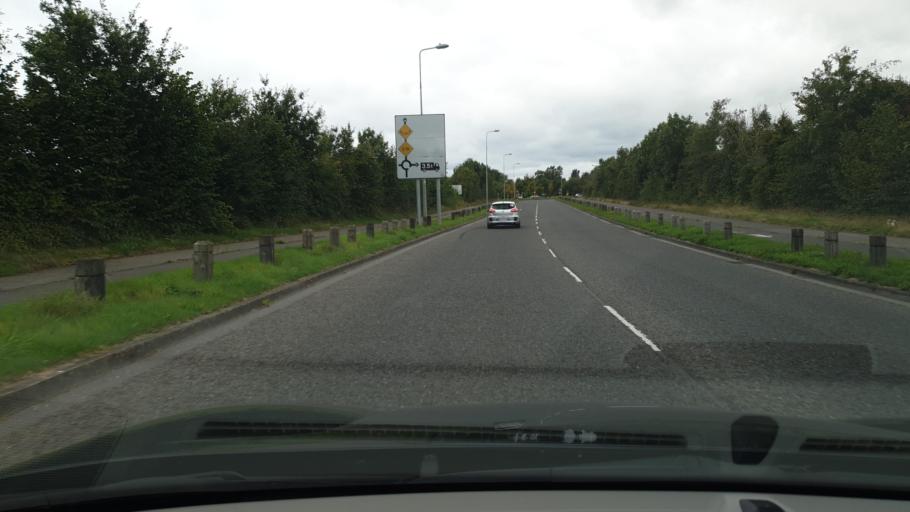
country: IE
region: Leinster
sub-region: Kildare
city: Naas
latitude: 53.2198
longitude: -6.6928
